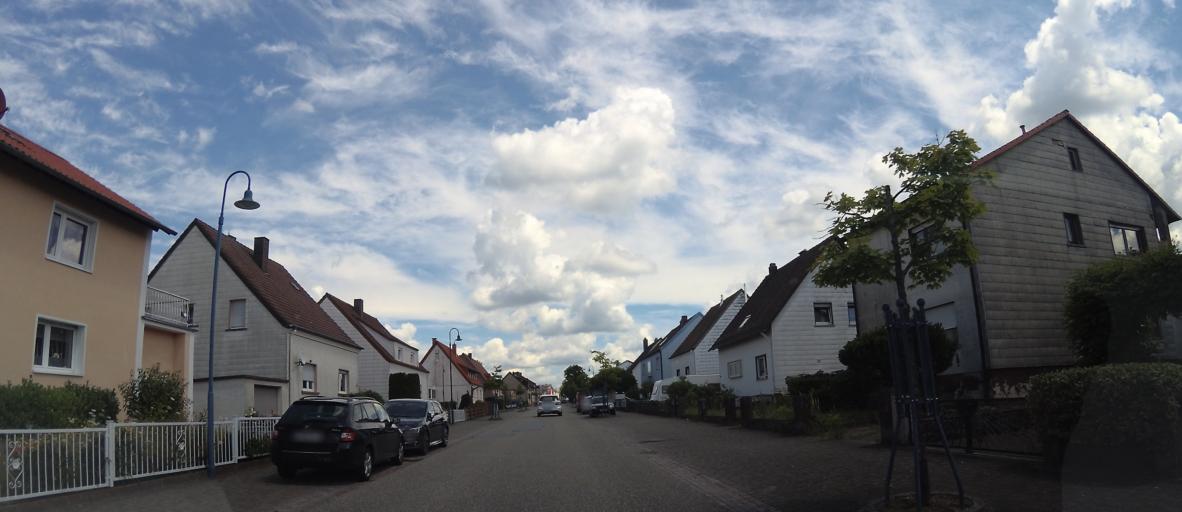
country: DE
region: Rheinland-Pfalz
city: Vinningen
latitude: 49.1531
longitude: 7.5489
